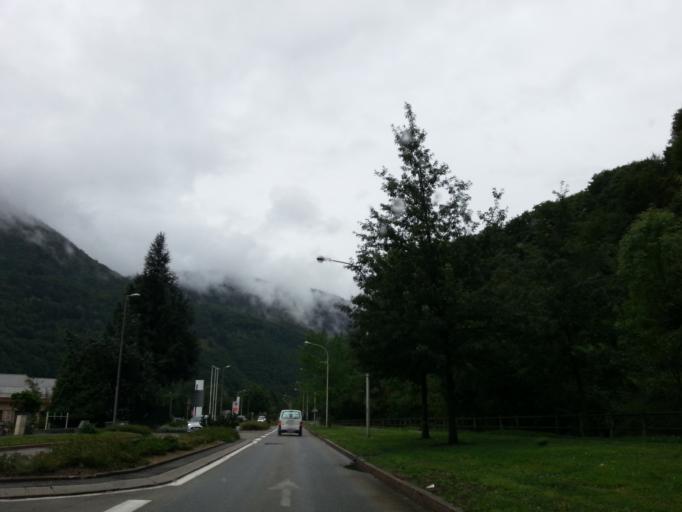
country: FR
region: Rhone-Alpes
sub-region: Departement de la Savoie
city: Ugine
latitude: 45.7433
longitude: 6.4216
